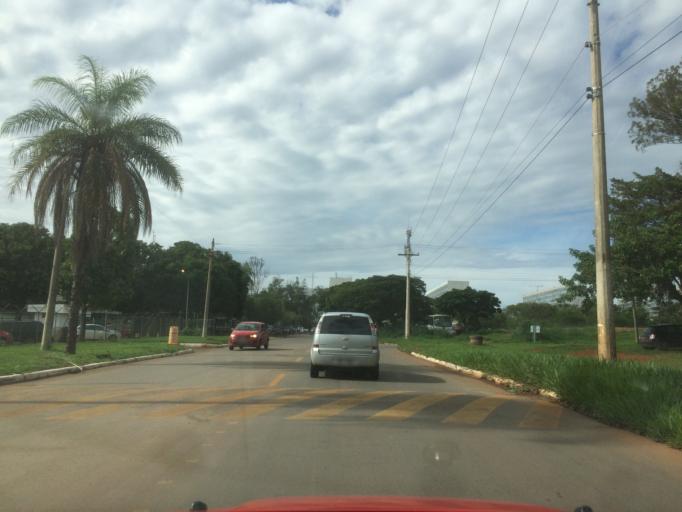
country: BR
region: Federal District
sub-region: Brasilia
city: Brasilia
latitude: -15.7922
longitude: -47.8655
